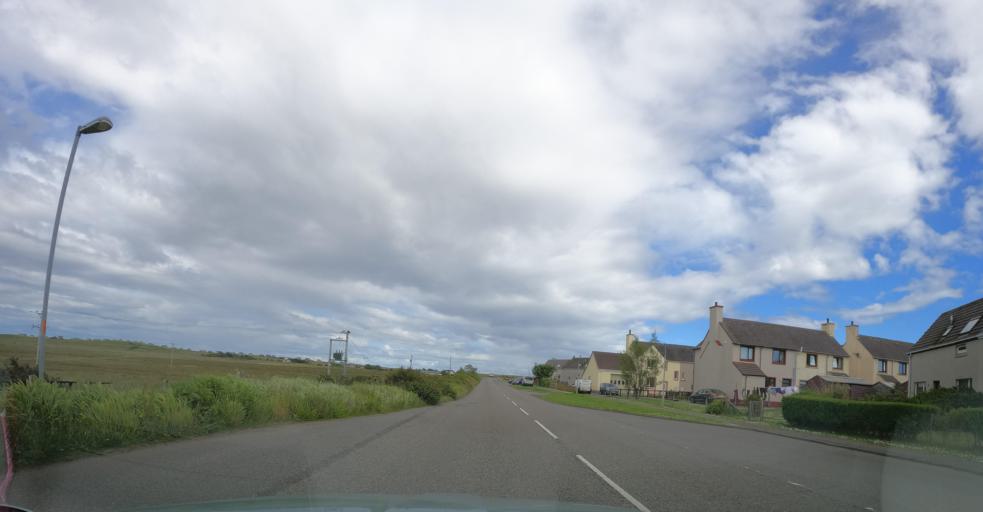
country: GB
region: Scotland
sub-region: Eilean Siar
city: Stornoway
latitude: 58.2087
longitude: -6.2605
